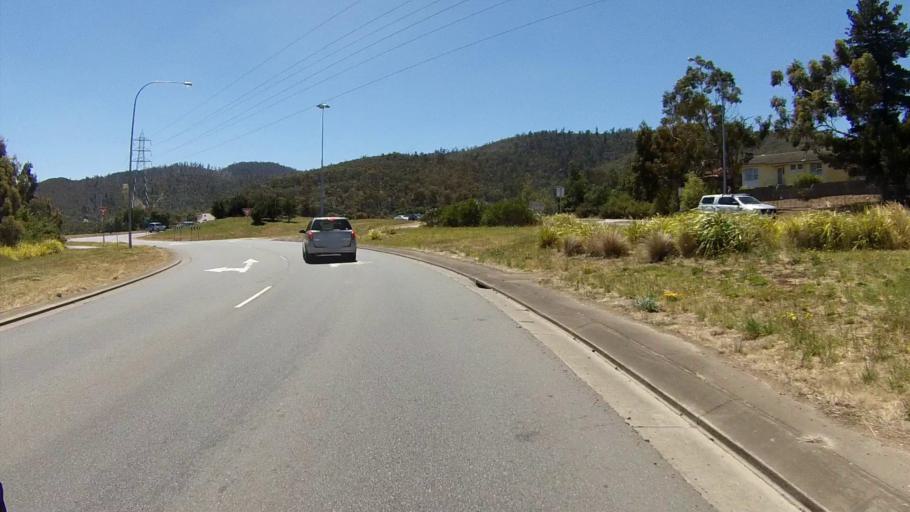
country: AU
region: Tasmania
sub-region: Clarence
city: Warrane
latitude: -42.8573
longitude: 147.3944
